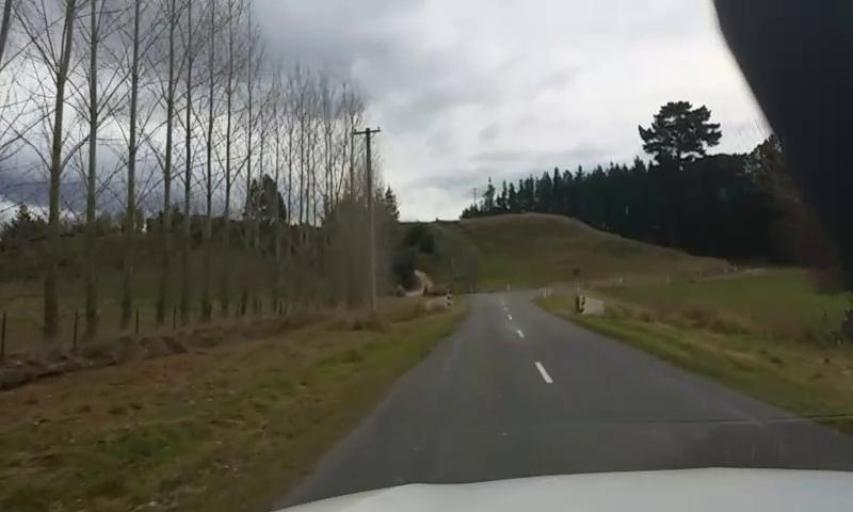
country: NZ
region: Canterbury
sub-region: Waimakariri District
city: Kaiapoi
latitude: -43.2994
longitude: 172.4378
